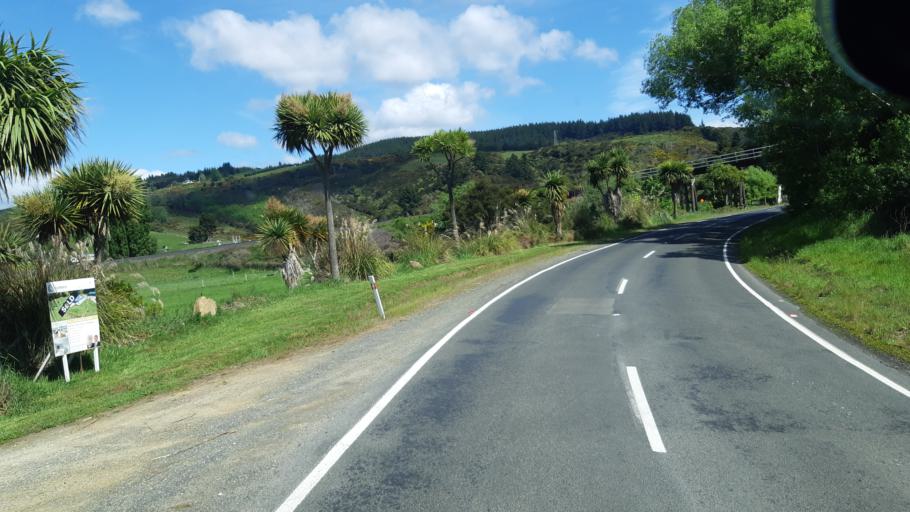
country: NZ
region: Otago
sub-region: Dunedin City
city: Portobello
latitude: -45.7165
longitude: 170.5741
